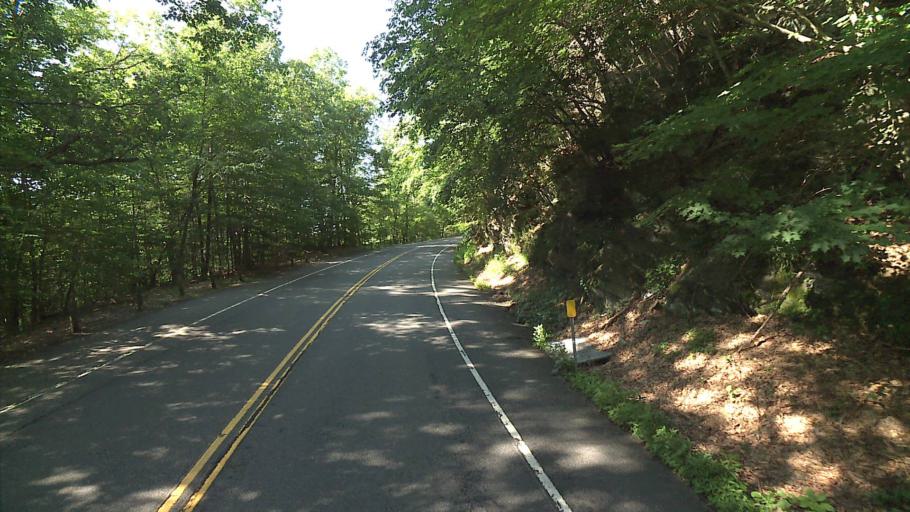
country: US
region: Massachusetts
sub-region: Hampden County
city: Granville
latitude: 42.0305
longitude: -72.9394
